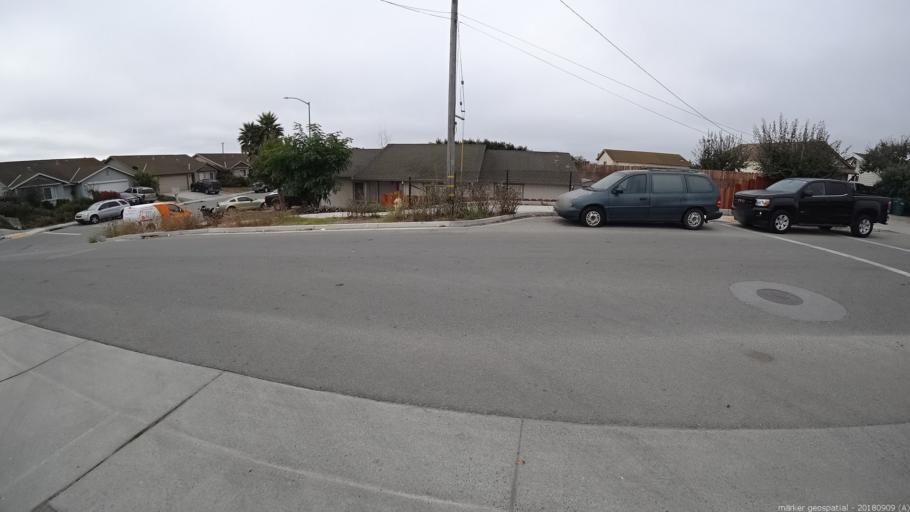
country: US
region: California
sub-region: Monterey County
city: Boronda
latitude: 36.6999
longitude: -121.6736
